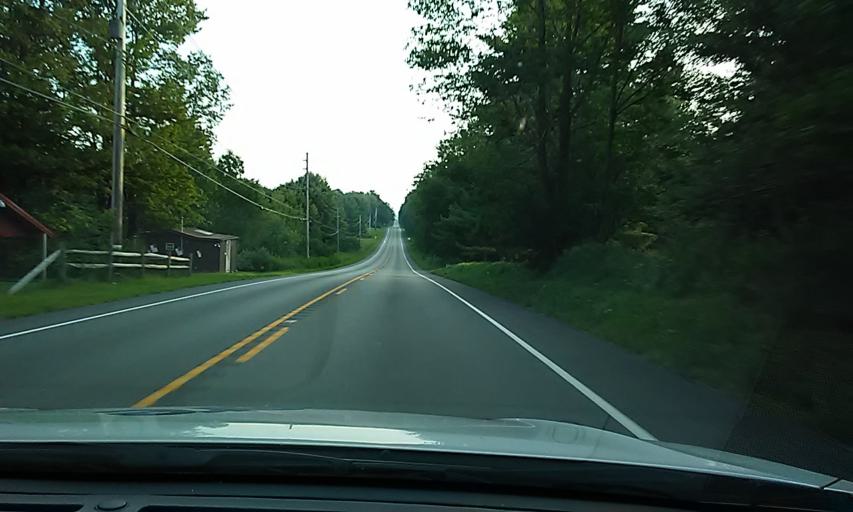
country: US
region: Pennsylvania
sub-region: Forest County
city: Marienville
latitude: 41.4972
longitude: -79.0862
